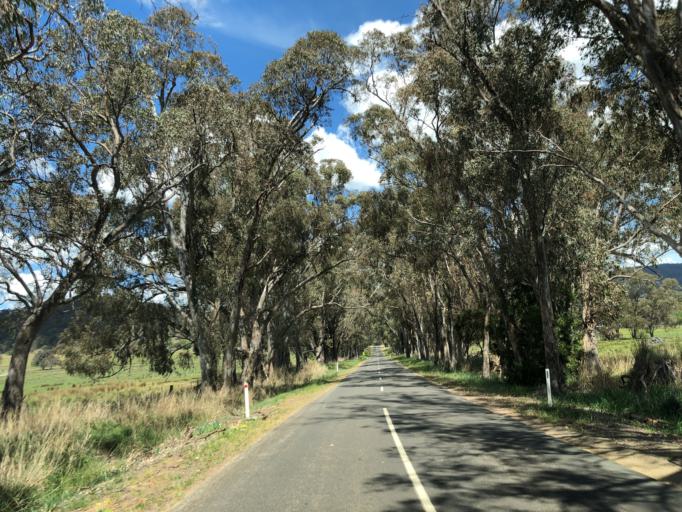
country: AU
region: Victoria
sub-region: Benalla
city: Benalla
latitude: -36.7457
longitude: 146.1183
